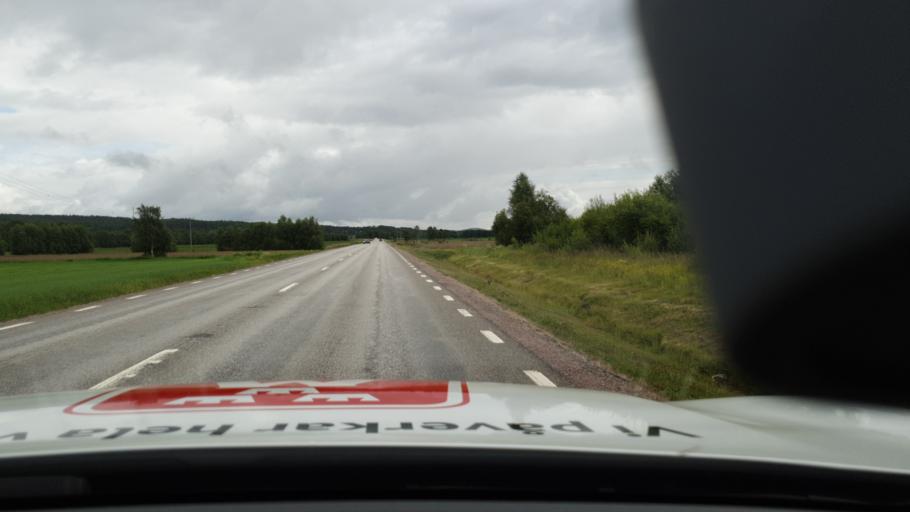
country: SE
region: Norrbotten
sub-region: Pitea Kommun
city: Rosvik
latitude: 65.5739
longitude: 21.7402
